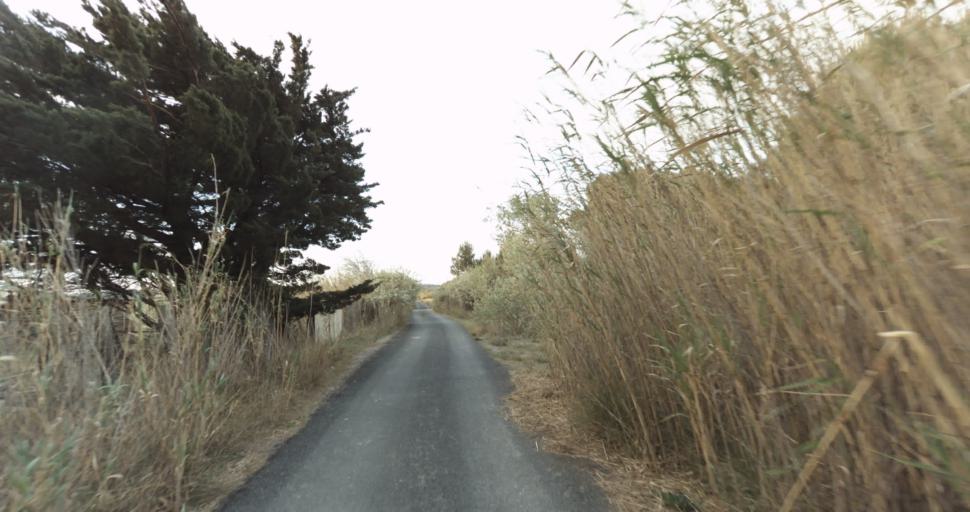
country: FR
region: Languedoc-Roussillon
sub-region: Departement de l'Aude
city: Leucate
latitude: 42.9480
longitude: 3.0301
